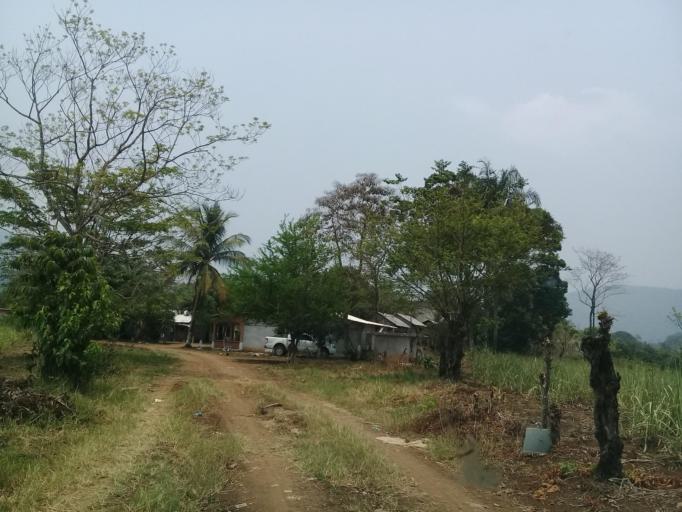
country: MX
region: Veracruz
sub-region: Tezonapa
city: Laguna Chica (Pueblo Nuevo)
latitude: 18.5396
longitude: -96.7372
